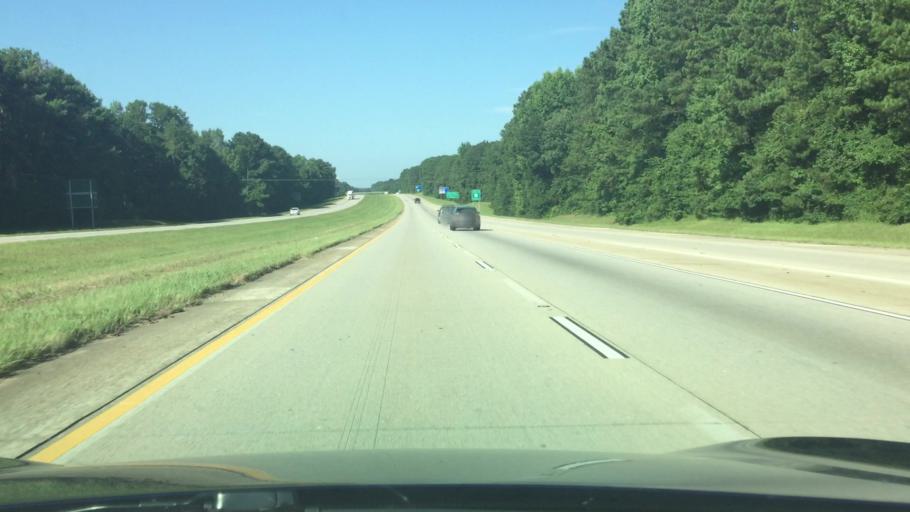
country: US
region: Georgia
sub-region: Troup County
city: La Grange
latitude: 32.9976
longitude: -85.0168
